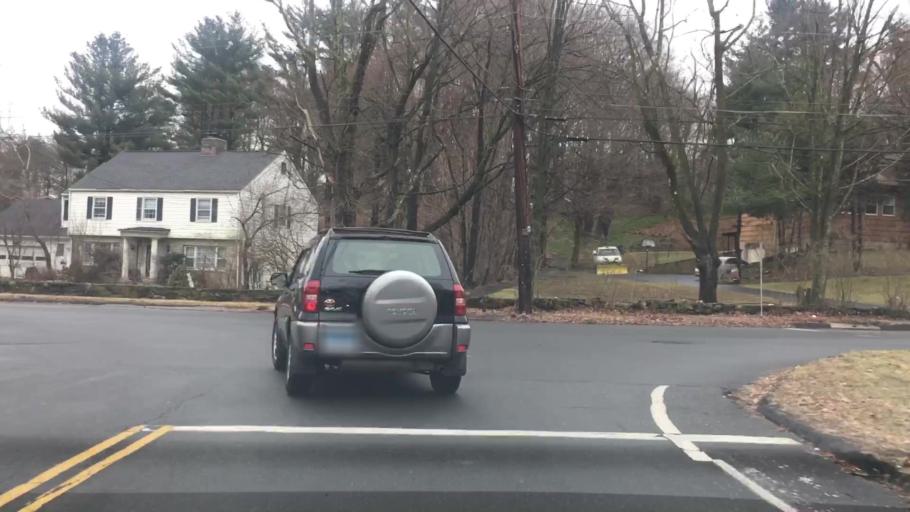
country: US
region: Connecticut
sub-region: Fairfield County
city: Danbury
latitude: 41.3818
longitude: -73.4637
